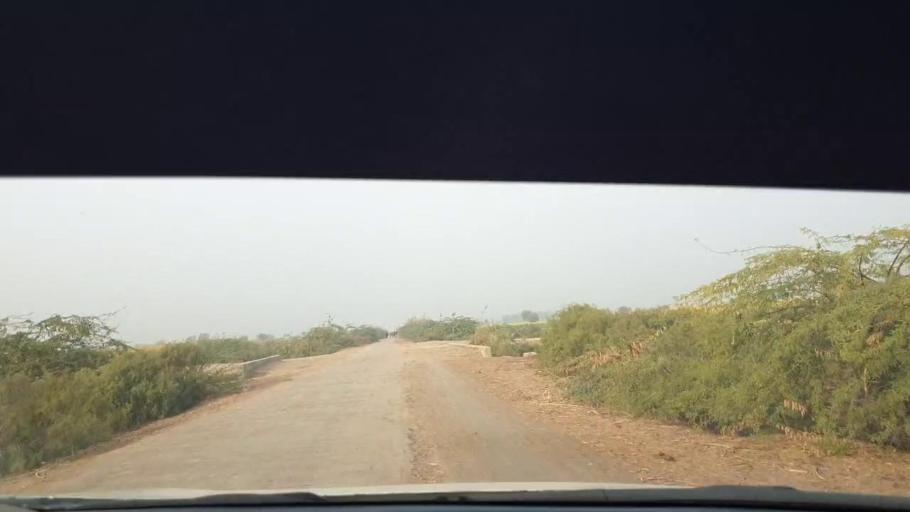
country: PK
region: Sindh
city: Berani
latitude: 25.8083
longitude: 68.8821
